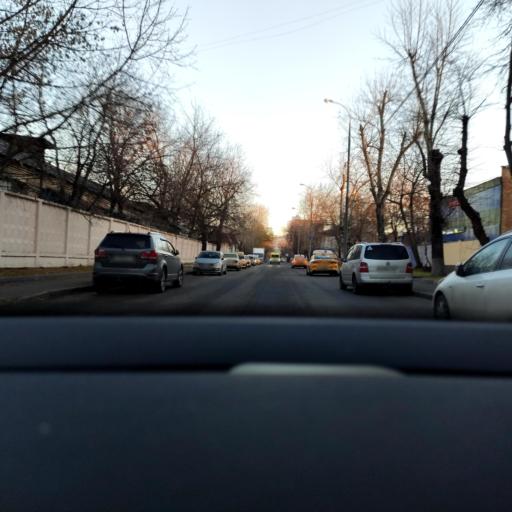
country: RU
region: Moscow
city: Ryazanskiy
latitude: 55.7214
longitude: 37.7553
